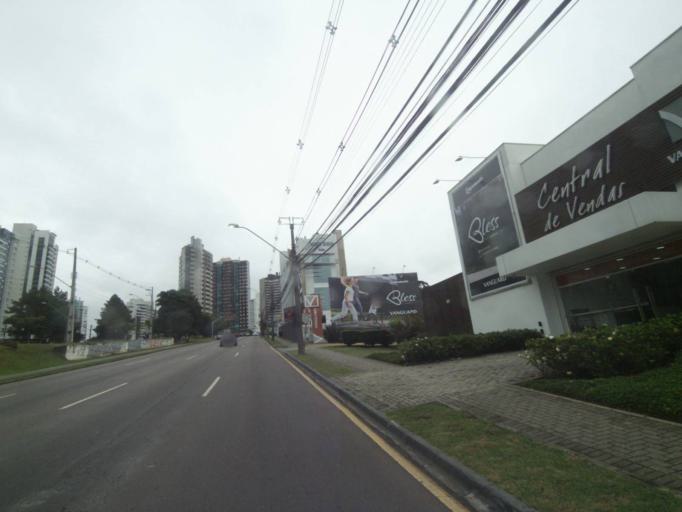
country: BR
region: Parana
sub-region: Curitiba
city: Curitiba
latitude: -25.4369
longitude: -49.3209
